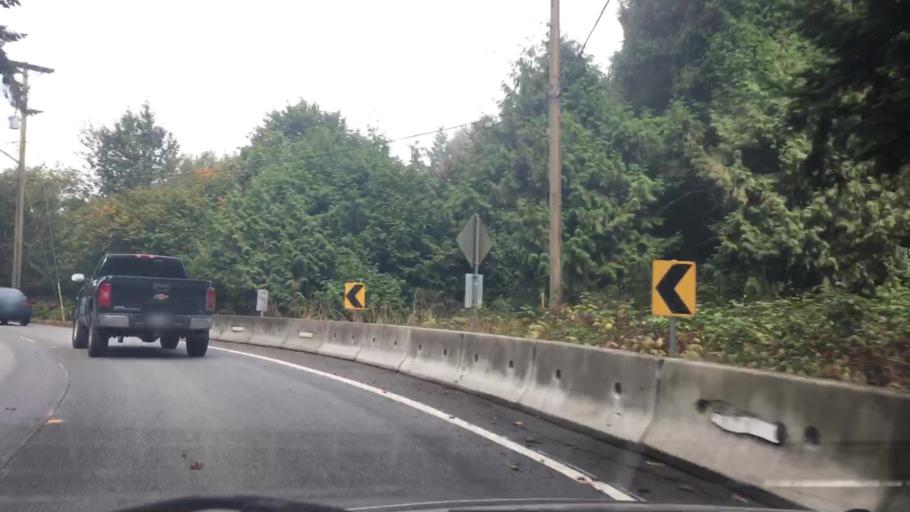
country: CA
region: British Columbia
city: Langley
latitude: 49.1040
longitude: -122.5537
